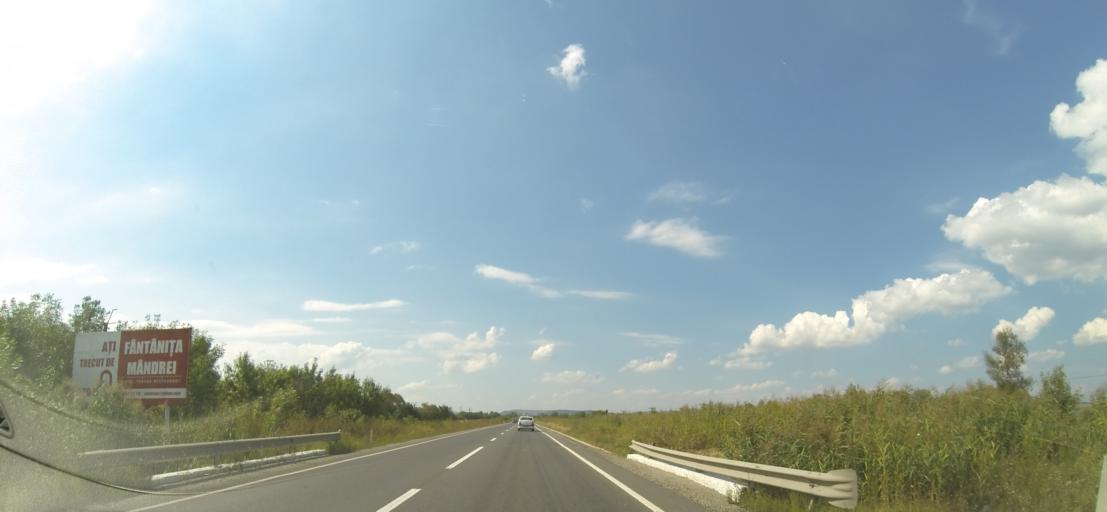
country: RO
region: Brasov
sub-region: Comuna Mandra
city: Mandra
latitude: 45.8284
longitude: 25.0271
